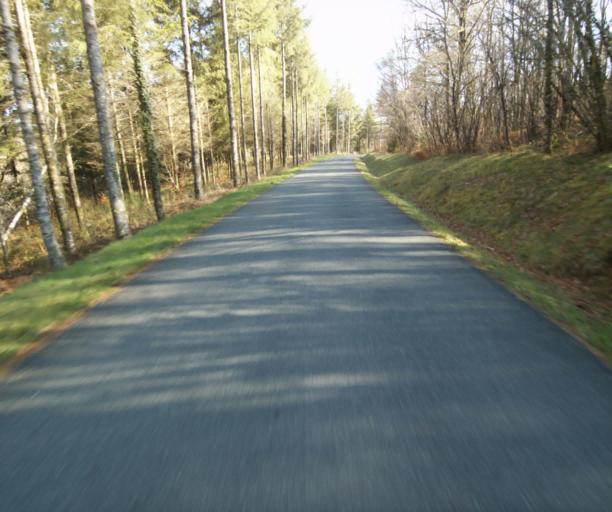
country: FR
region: Limousin
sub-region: Departement de la Correze
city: Correze
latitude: 45.3085
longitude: 1.8813
